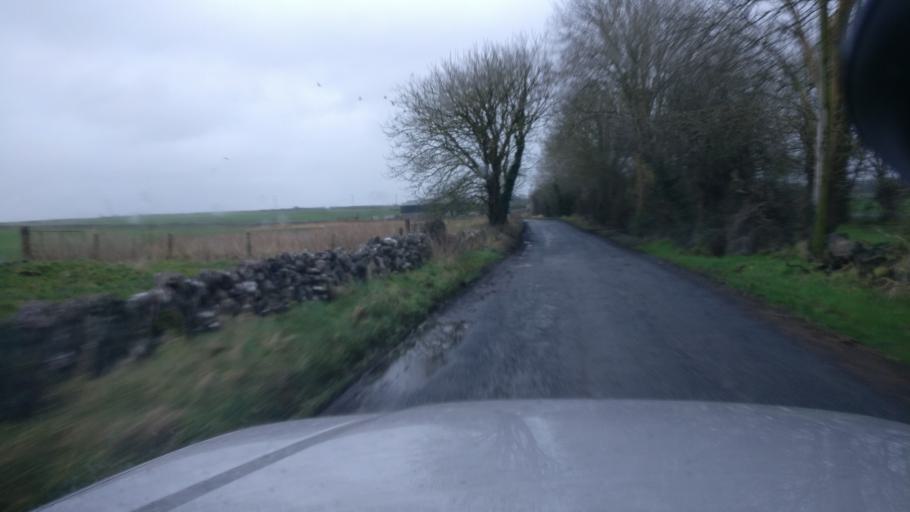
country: IE
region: Connaught
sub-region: County Galway
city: Loughrea
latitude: 53.2302
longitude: -8.6126
